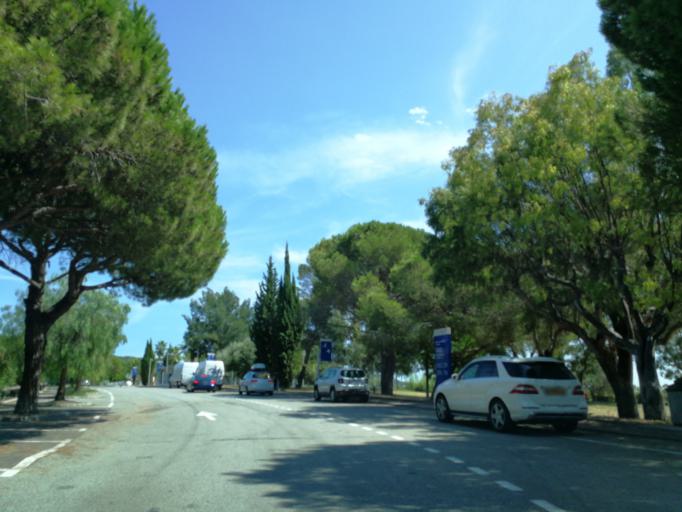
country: FR
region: Provence-Alpes-Cote d'Azur
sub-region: Departement des Alpes-Maritimes
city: Le Cannet
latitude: 43.5815
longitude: 7.0148
